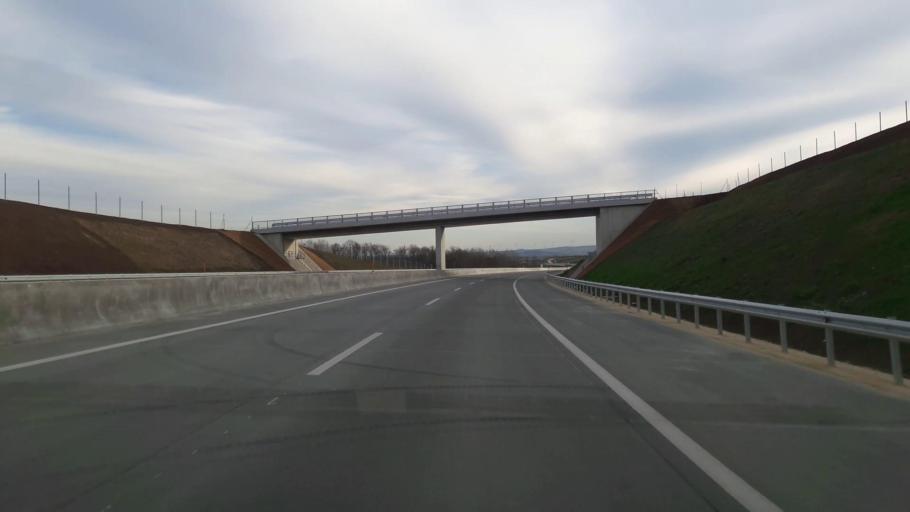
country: AT
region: Lower Austria
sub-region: Politischer Bezirk Mistelbach
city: Herrnbaumgarten
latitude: 48.6733
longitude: 16.6733
